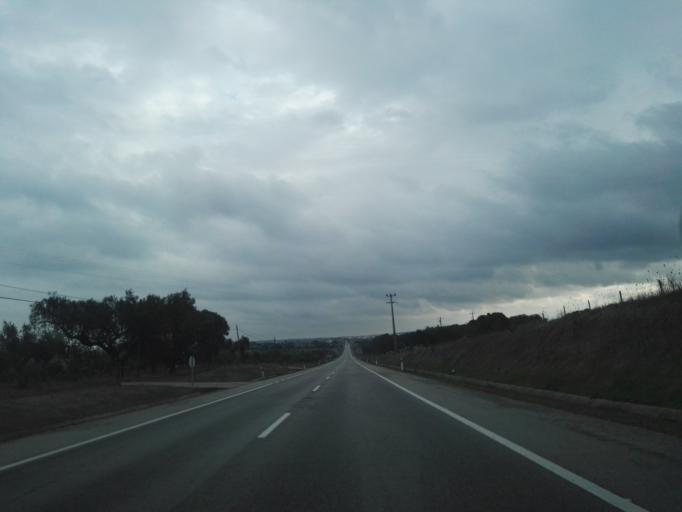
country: PT
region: Portalegre
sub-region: Arronches
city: Arronches
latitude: 39.1442
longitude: -7.3027
